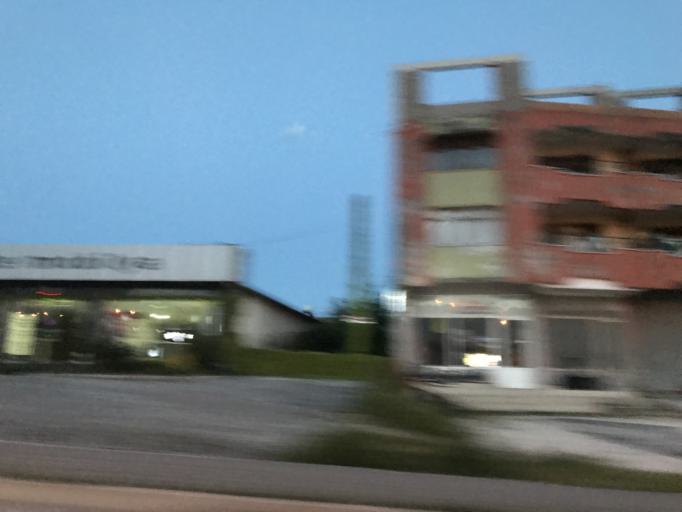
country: TR
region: Hatay
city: Asagiokcular
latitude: 36.1842
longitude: 36.1206
